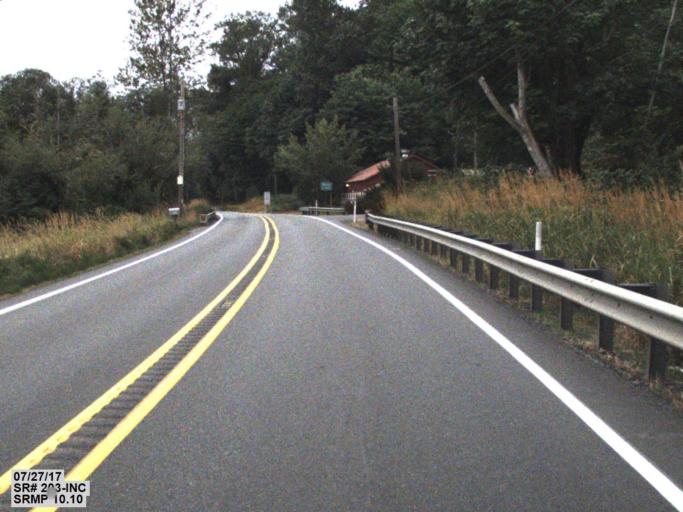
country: US
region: Washington
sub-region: King County
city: Lake Marcel-Stillwater
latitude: 47.6909
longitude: -121.9445
